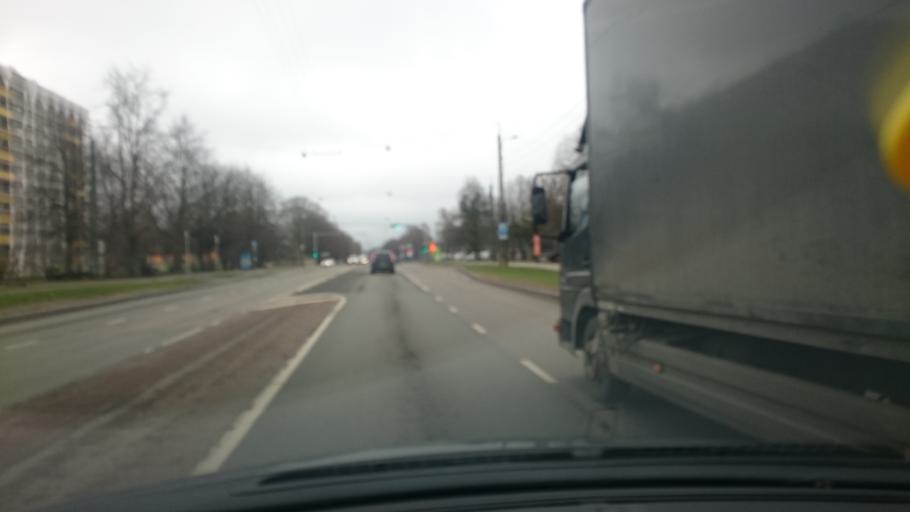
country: EE
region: Harju
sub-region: Tallinna linn
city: Tallinn
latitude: 59.4405
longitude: 24.7069
